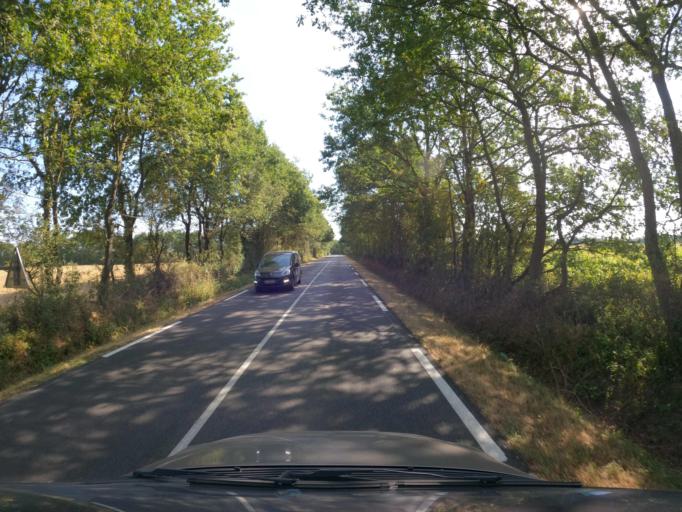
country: FR
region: Pays de la Loire
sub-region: Departement de la Vendee
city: Saint-Christophe-du-Ligneron
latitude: 46.8031
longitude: -1.7834
